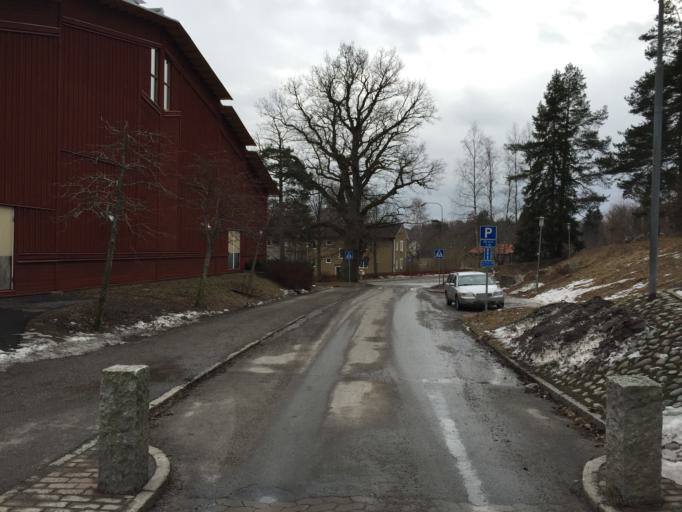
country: SE
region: Stockholm
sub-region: Salems Kommun
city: Ronninge
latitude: 59.2011
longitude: 17.7325
